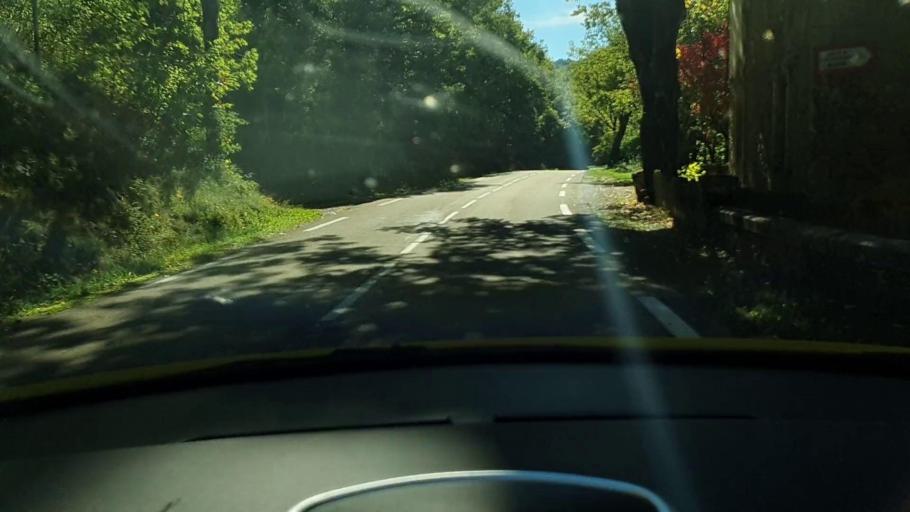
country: FR
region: Languedoc-Roussillon
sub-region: Departement du Gard
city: Le Vigan
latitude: 43.9722
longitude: 3.4146
